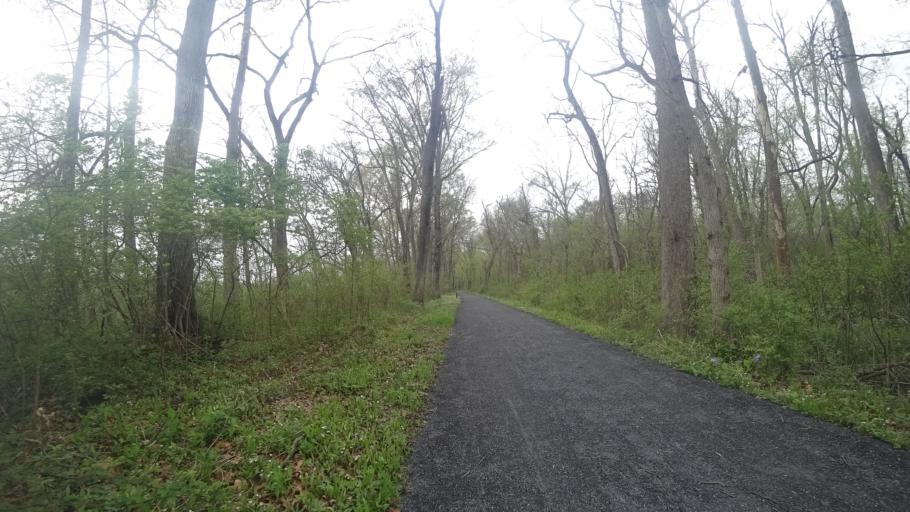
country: US
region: Virginia
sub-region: Loudoun County
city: Countryside
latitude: 39.0697
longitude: -77.3984
